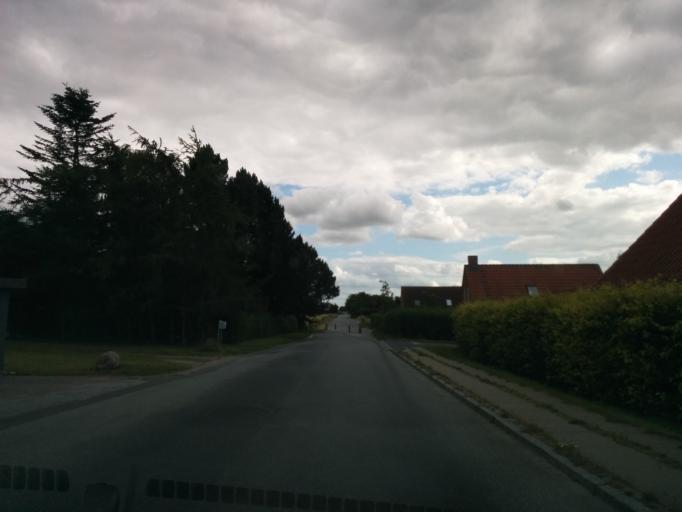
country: DK
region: Central Jutland
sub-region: Arhus Kommune
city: Kolt
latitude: 56.1243
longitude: 10.0647
